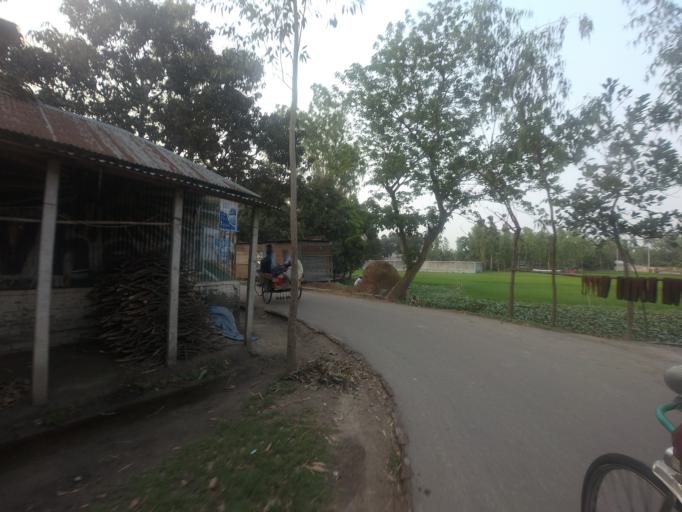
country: BD
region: Rajshahi
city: Sirajganj
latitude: 24.3320
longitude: 89.6915
